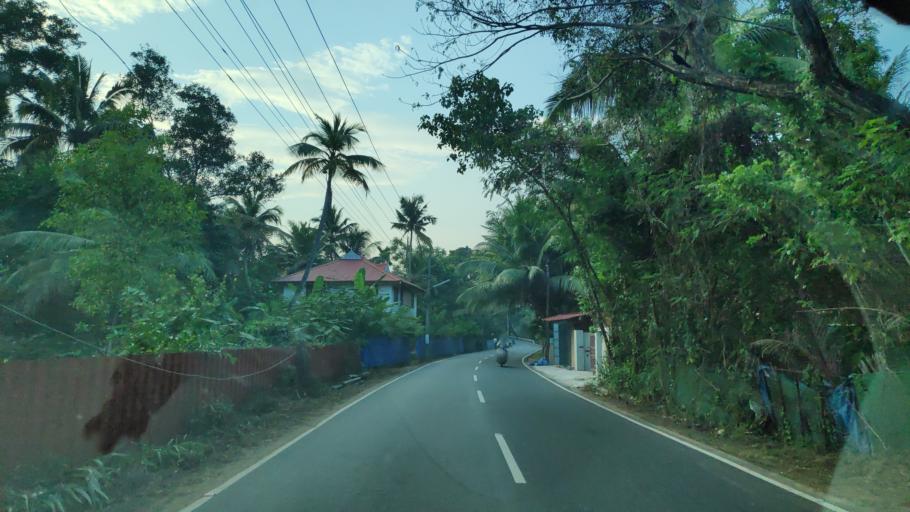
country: IN
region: Kerala
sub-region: Alappuzha
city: Shertallai
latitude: 9.6767
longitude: 76.3801
